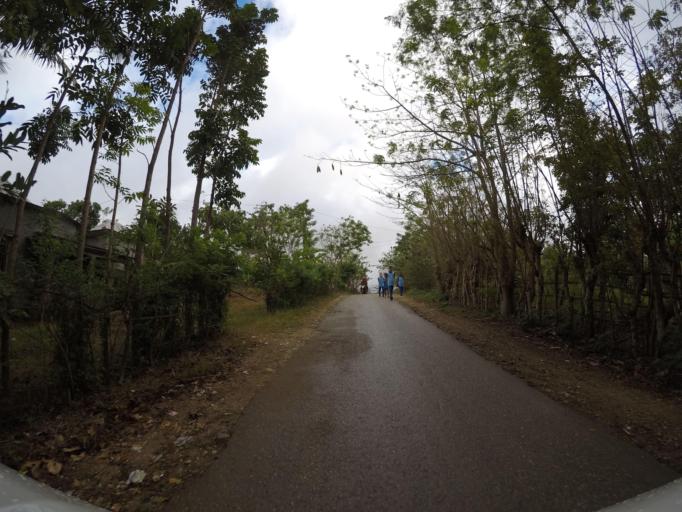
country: TL
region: Lautem
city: Lospalos
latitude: -8.5257
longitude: 126.9878
